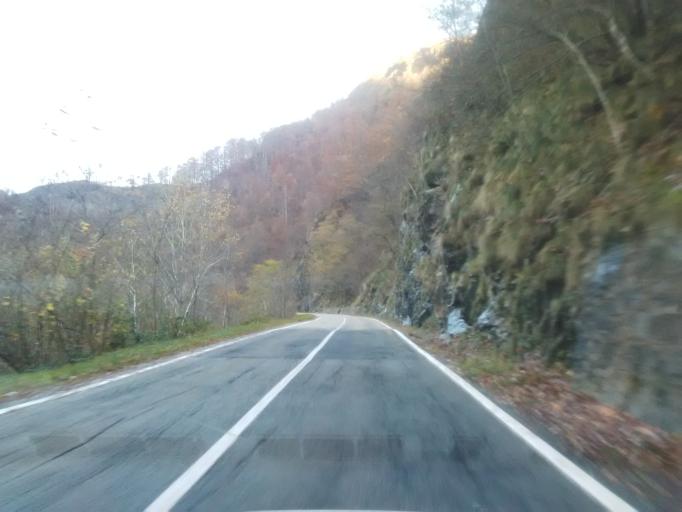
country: IT
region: Piedmont
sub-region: Provincia di Vercelli
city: Cervatto
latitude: 45.8739
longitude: 8.1820
